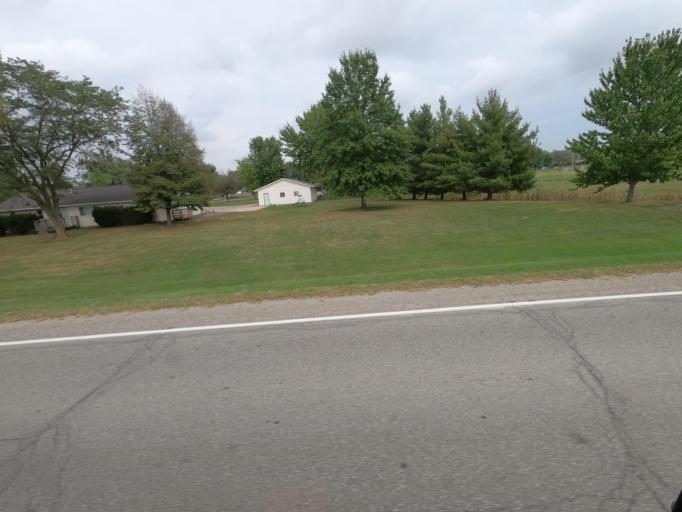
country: US
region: Iowa
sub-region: Wapello County
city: Ottumwa
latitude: 40.9140
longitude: -92.2150
